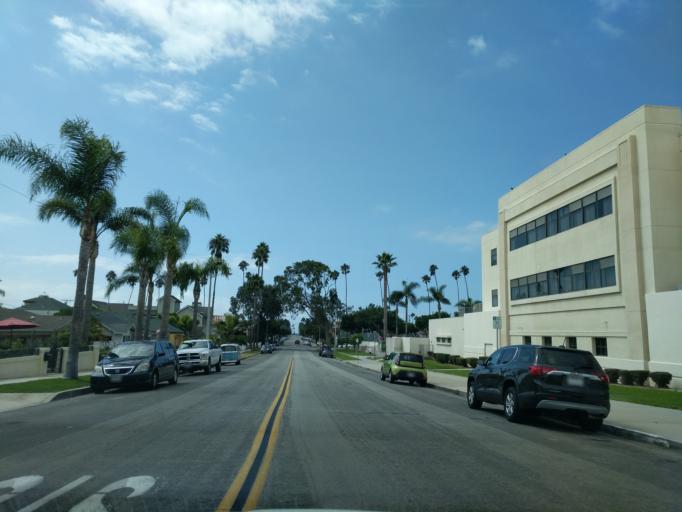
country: US
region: California
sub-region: Orange County
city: Huntington Beach
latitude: 33.6693
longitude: -118.0036
